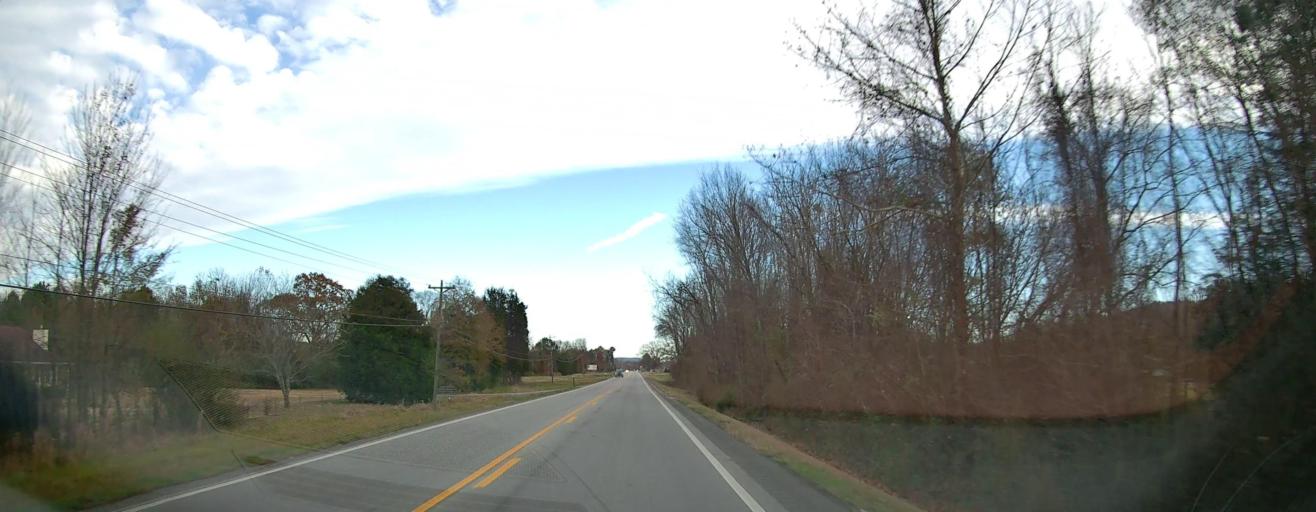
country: US
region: Alabama
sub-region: Morgan County
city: Falkville
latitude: 34.4194
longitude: -86.7108
